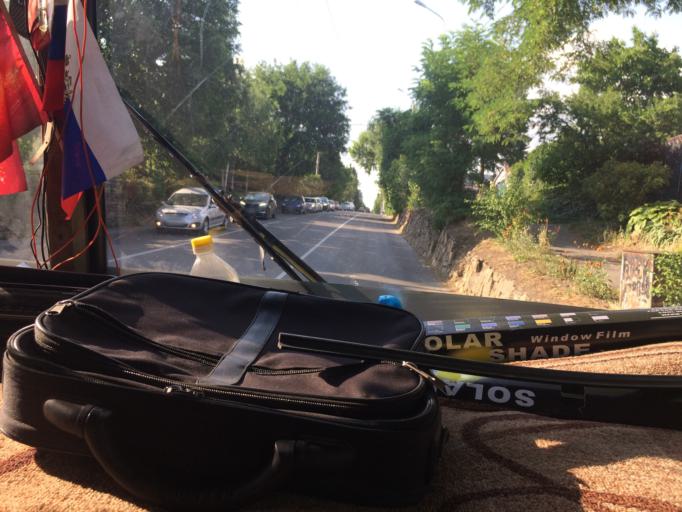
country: RU
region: Stavropol'skiy
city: Stavropol'
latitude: 45.0264
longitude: 41.9533
